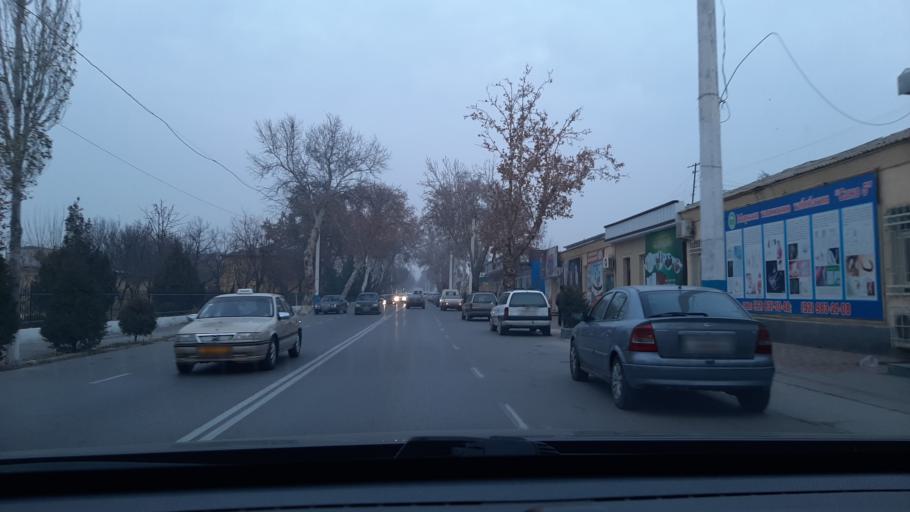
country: TJ
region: Viloyati Sughd
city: Khujand
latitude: 40.2742
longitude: 69.6071
